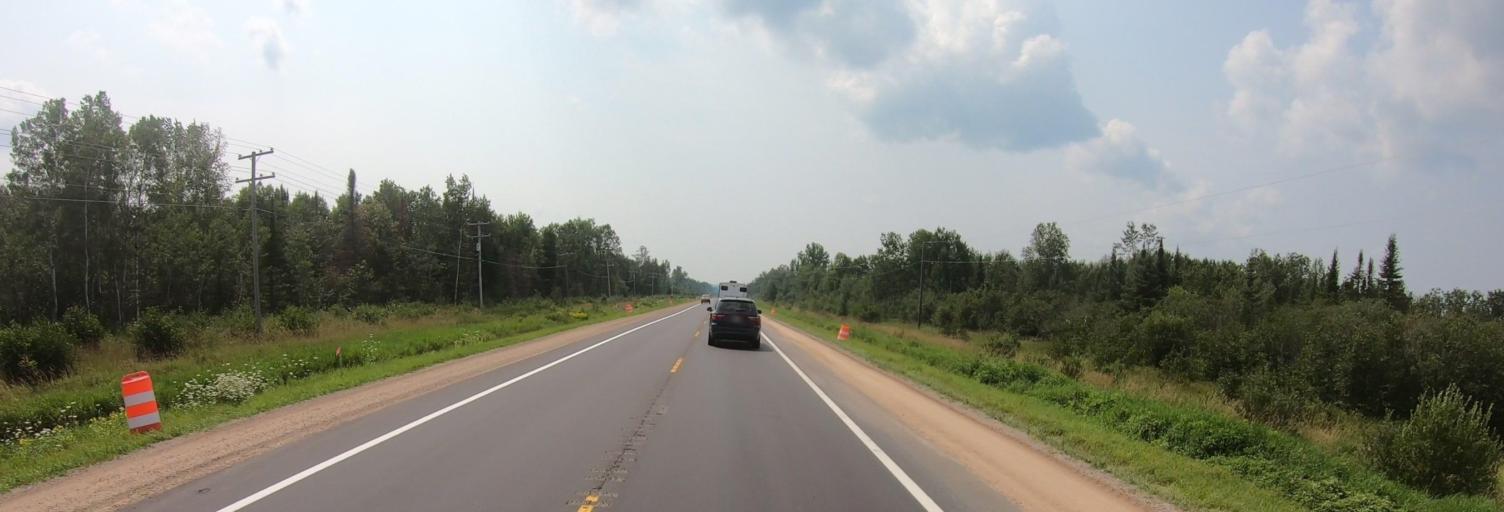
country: US
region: Michigan
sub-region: Luce County
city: Newberry
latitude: 46.3958
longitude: -85.5099
